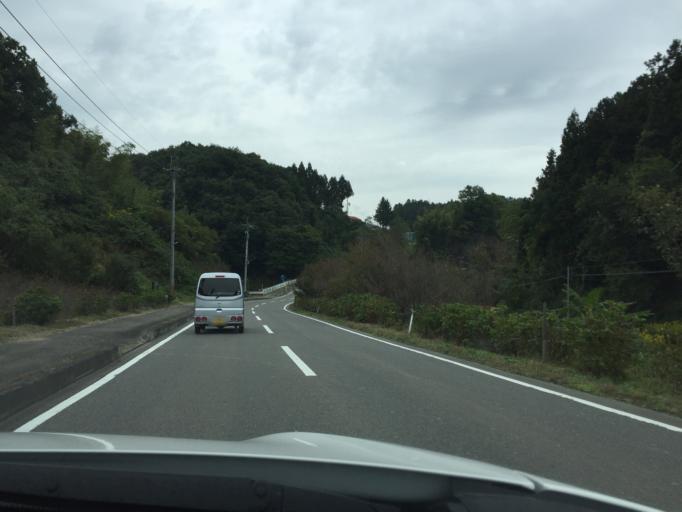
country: JP
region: Fukushima
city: Nihommatsu
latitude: 37.5848
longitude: 140.5560
